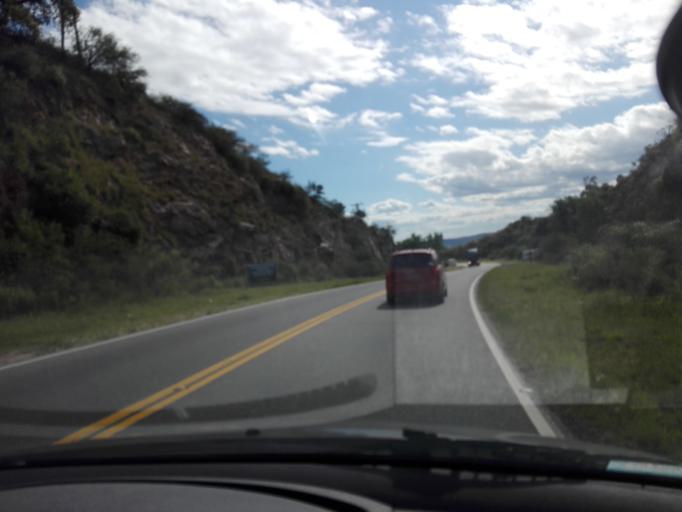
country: AR
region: Cordoba
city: Mina Clavero
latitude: -31.7600
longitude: -64.9599
